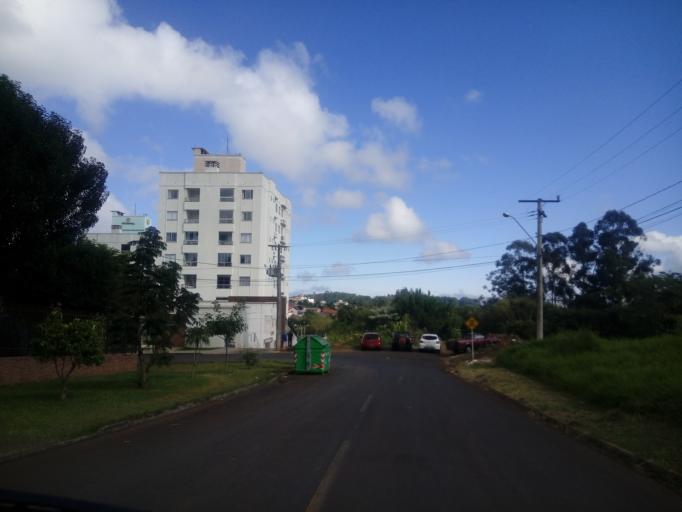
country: BR
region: Santa Catarina
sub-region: Chapeco
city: Chapeco
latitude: -27.1133
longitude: -52.6200
